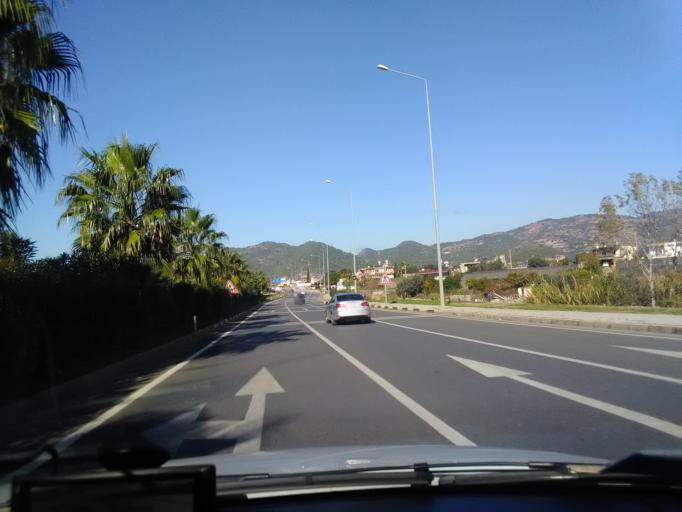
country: TR
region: Antalya
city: Gazipasa
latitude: 36.2877
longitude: 32.2948
